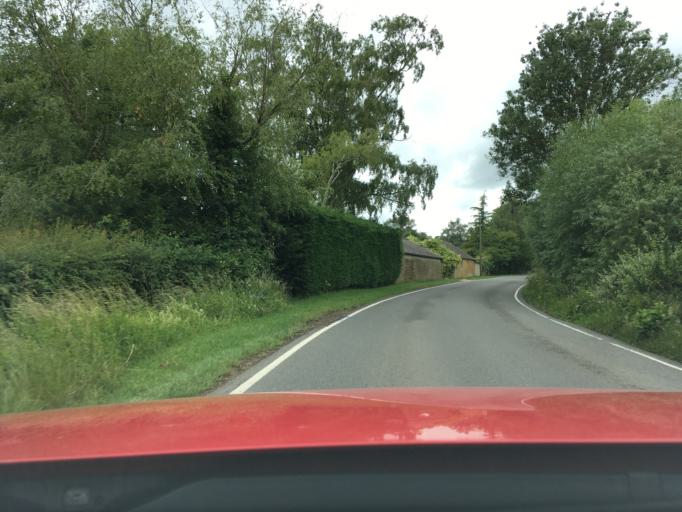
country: GB
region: England
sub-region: Warwickshire
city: Shipston on Stour
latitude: 52.0930
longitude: -1.6790
